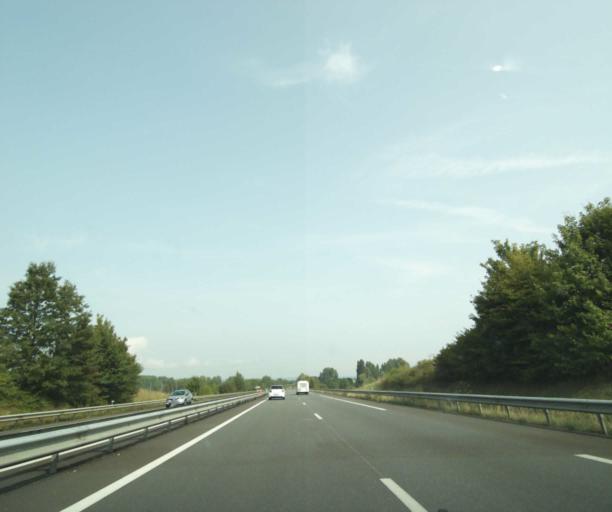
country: FR
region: Pays de la Loire
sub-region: Departement de la Sarthe
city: Saint-Paterne
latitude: 48.4338
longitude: 0.1372
